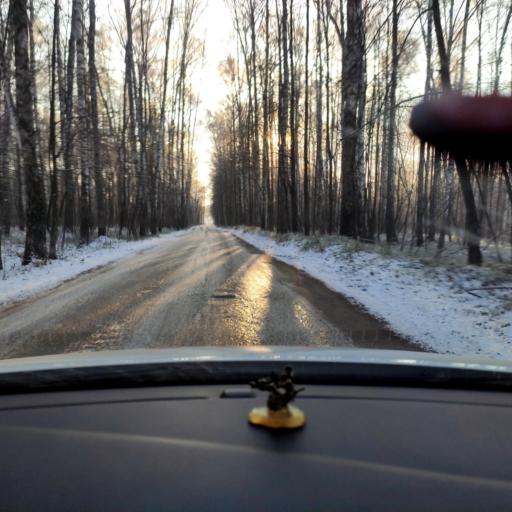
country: RU
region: Tatarstan
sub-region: Gorod Kazan'
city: Kazan
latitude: 55.6756
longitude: 49.1019
